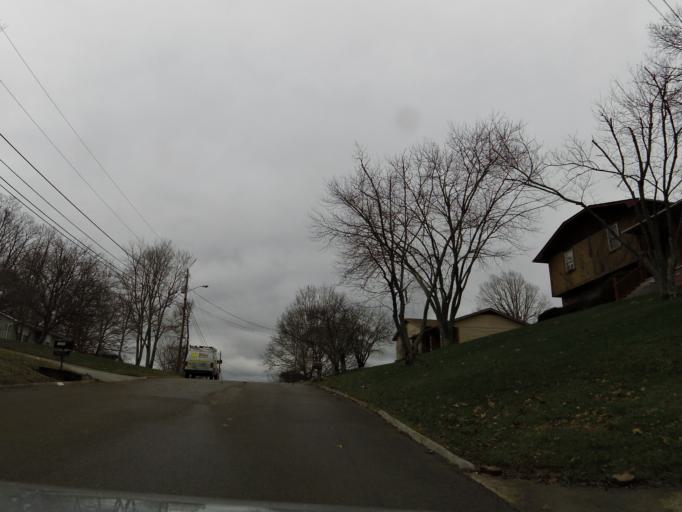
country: US
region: Tennessee
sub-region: Knox County
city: Knoxville
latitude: 35.9926
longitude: -84.0223
